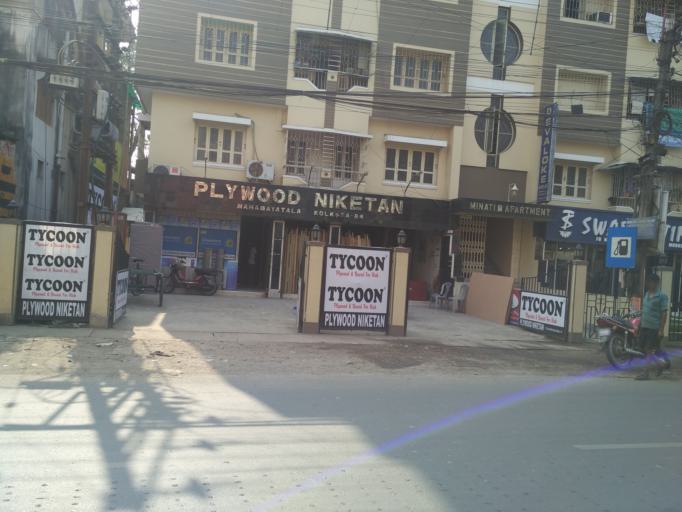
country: IN
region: West Bengal
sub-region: Kolkata
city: Kolkata
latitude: 22.4534
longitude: 88.3883
